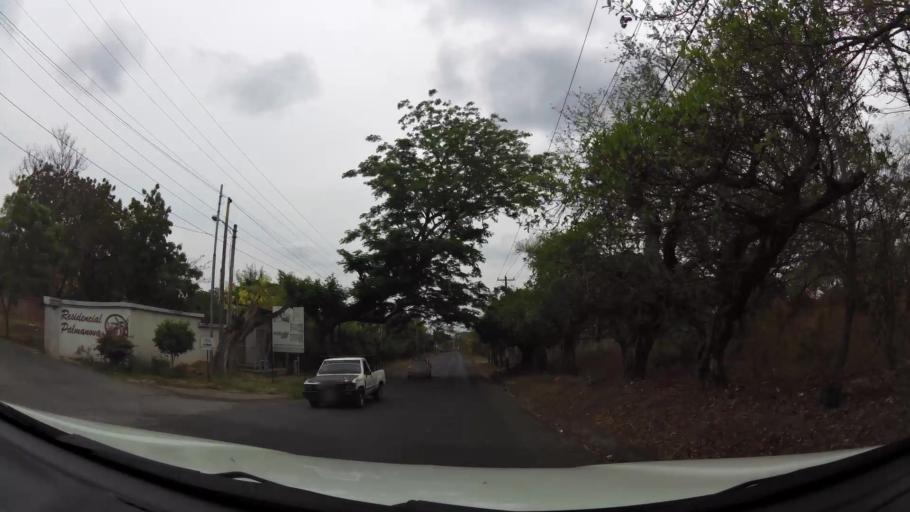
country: NI
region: Masaya
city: Ticuantepe
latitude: 12.0728
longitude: -86.1806
